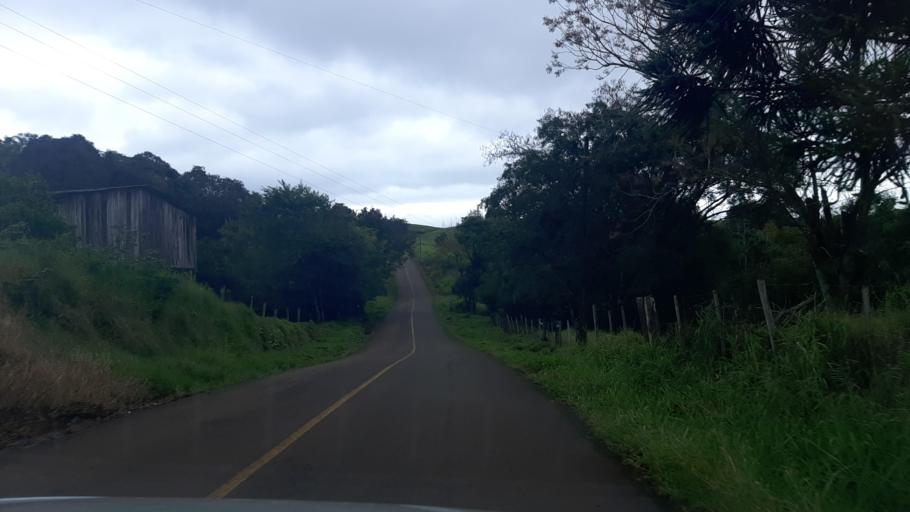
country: BR
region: Parana
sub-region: Ampere
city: Ampere
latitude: -26.0384
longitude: -53.4901
